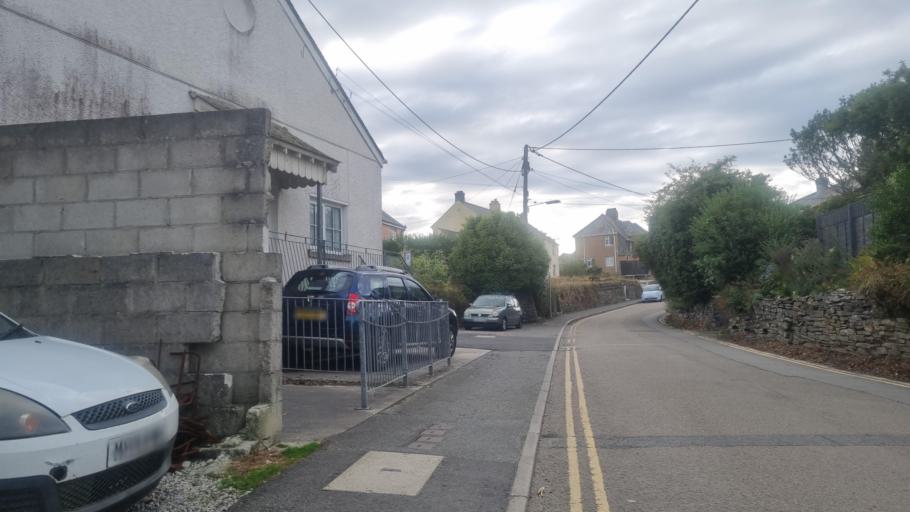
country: GB
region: England
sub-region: Cornwall
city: Tintagel
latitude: 50.6212
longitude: -4.7281
